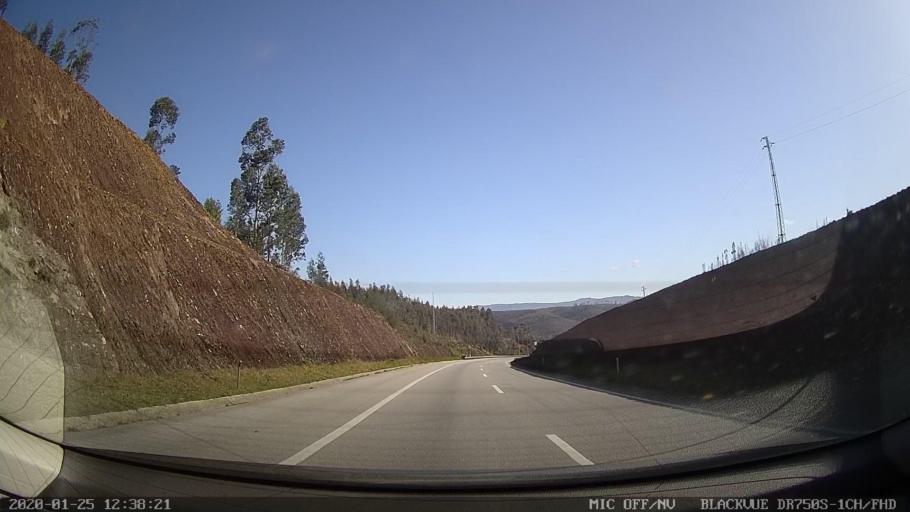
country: PT
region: Aveiro
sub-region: Albergaria-A-Velha
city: Albergaria-a-Velha
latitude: 40.6776
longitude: -8.4509
